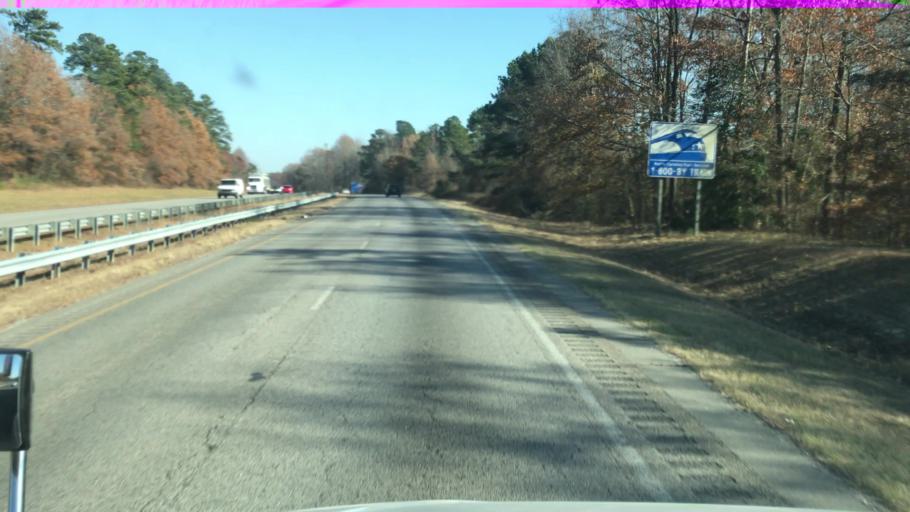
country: US
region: North Carolina
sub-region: Nash County
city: Nashville
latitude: 35.9767
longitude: -77.9136
